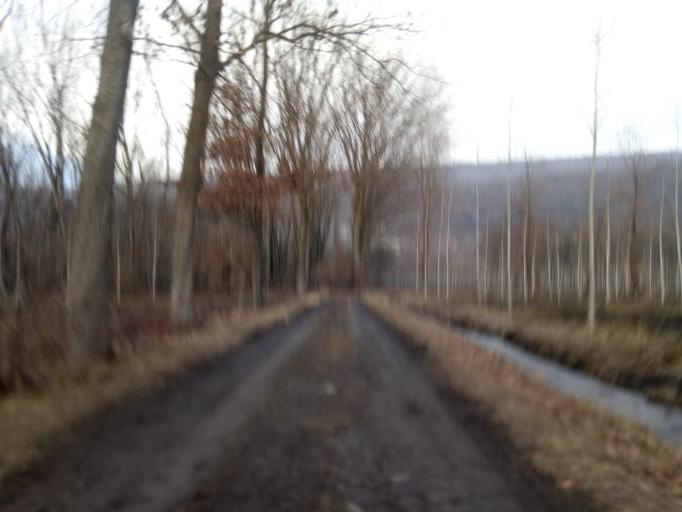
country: IT
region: Piedmont
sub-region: Provincia di Torino
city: Cascinette d'Ivrea
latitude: 45.4870
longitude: 7.9176
